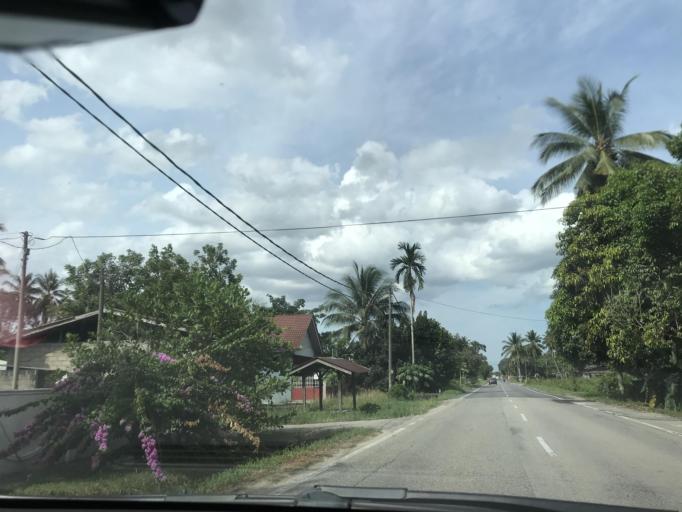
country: MY
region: Kelantan
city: Kampung Lemal
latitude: 6.0340
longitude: 102.1700
